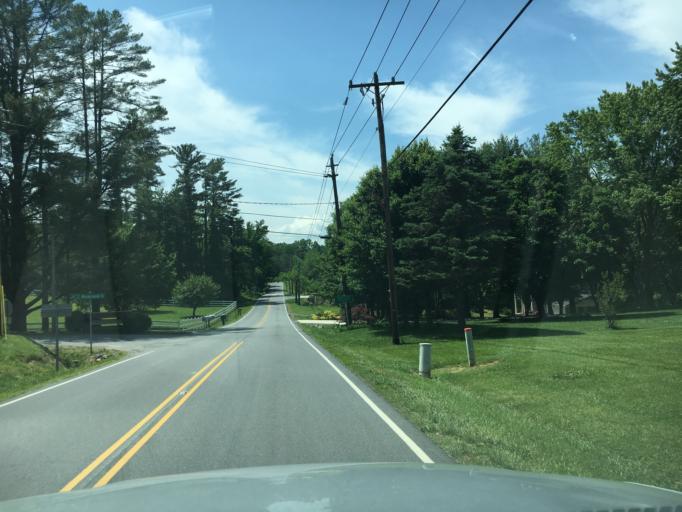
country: US
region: North Carolina
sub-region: Henderson County
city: Mountain Home
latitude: 35.3811
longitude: -82.5196
